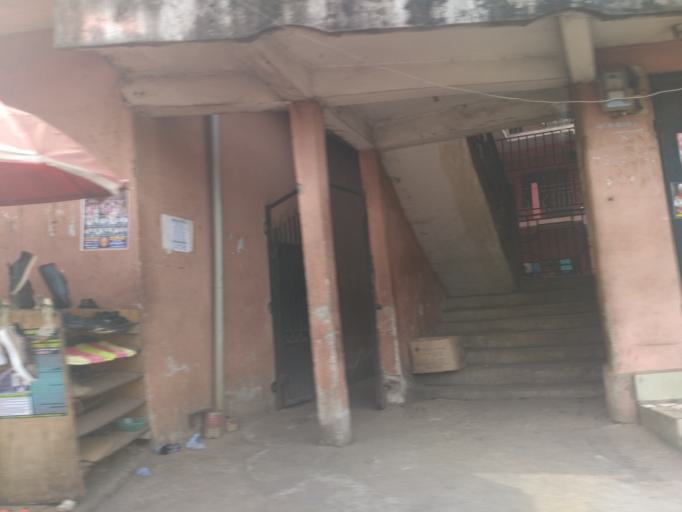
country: GH
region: Ashanti
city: Kumasi
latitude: 6.6997
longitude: -1.6315
